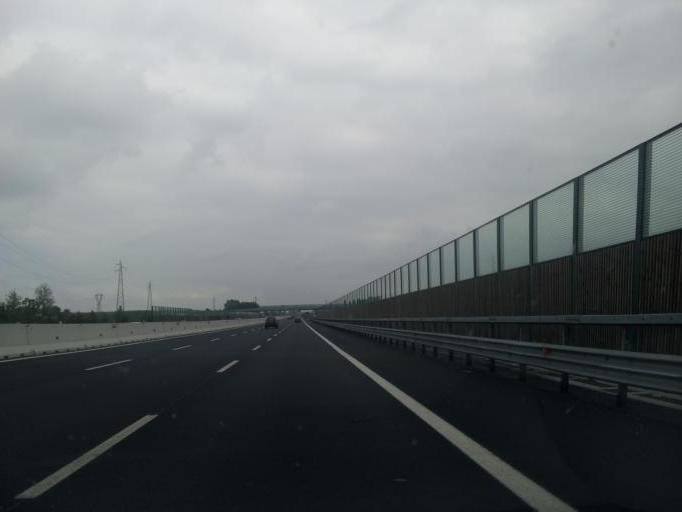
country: IT
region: Veneto
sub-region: Provincia di Treviso
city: Musestre
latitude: 45.5926
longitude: 12.3737
